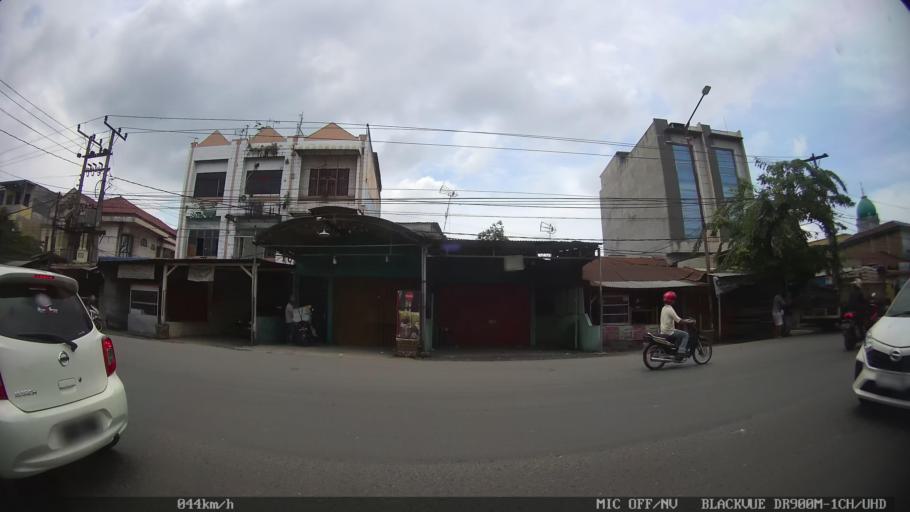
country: ID
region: North Sumatra
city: Labuhan Deli
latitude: 3.6888
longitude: 98.6682
